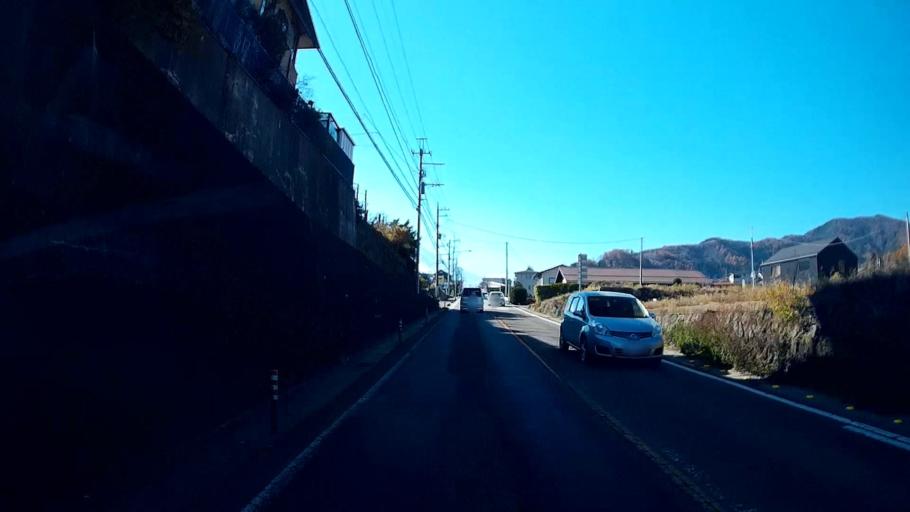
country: JP
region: Yamanashi
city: Otsuki
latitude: 35.5151
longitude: 138.8335
